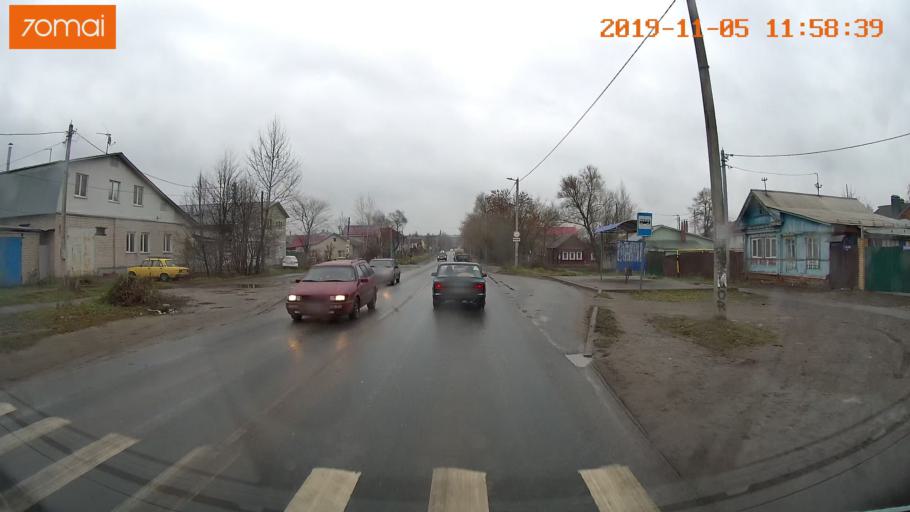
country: RU
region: Ivanovo
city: Kokhma
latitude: 56.9806
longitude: 41.0411
